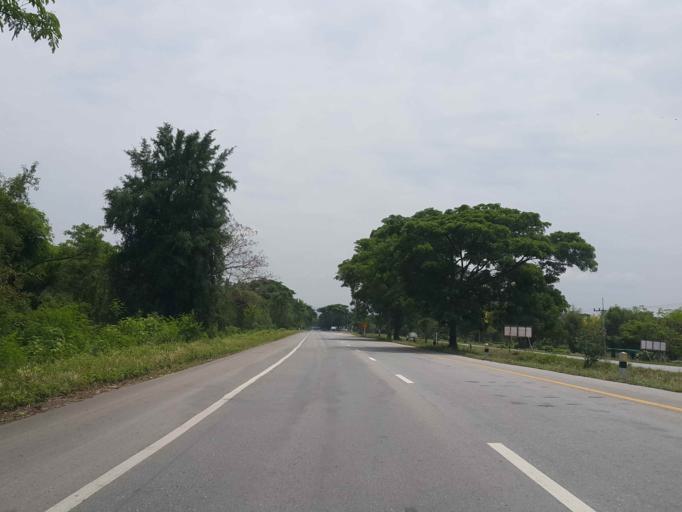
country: TH
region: Lampang
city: Sop Prap
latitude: 17.9125
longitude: 99.3420
